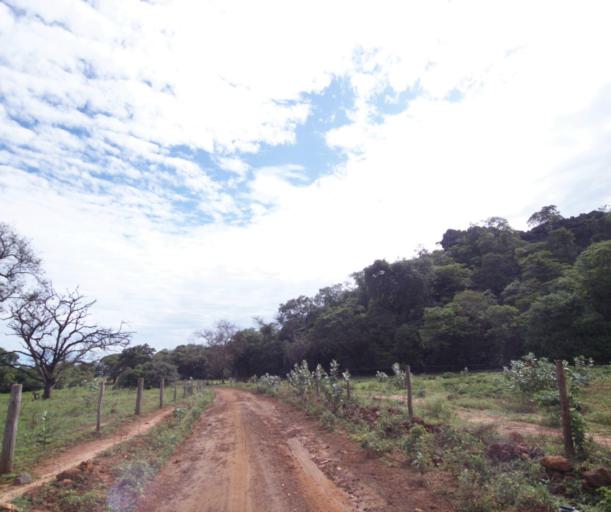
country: BR
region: Bahia
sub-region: Carinhanha
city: Carinhanha
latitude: -14.2421
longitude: -44.4137
